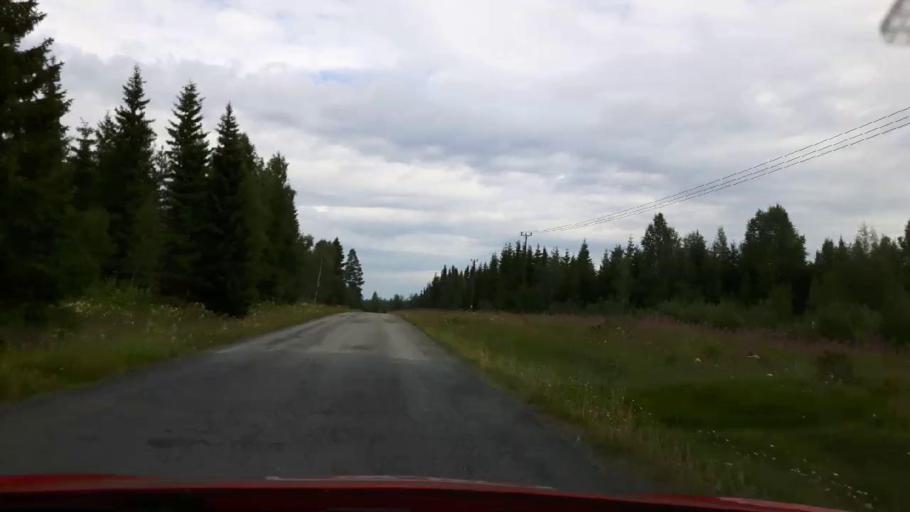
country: SE
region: Jaemtland
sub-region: Stroemsunds Kommun
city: Stroemsund
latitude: 63.5332
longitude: 15.3542
